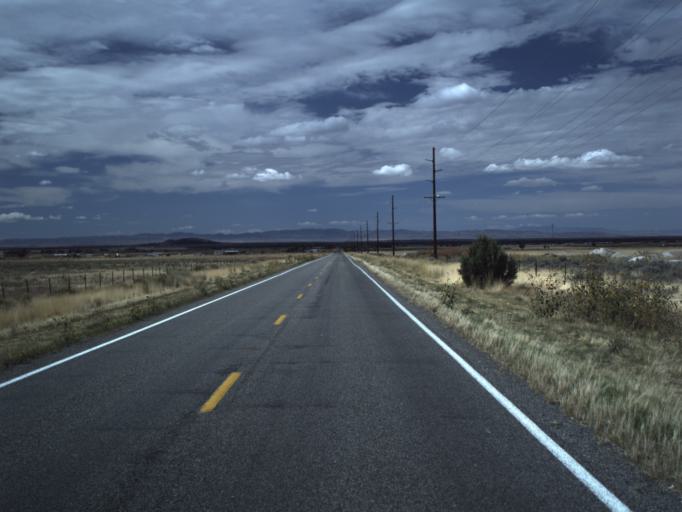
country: US
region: Utah
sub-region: Millard County
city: Fillmore
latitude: 38.9792
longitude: -112.3813
